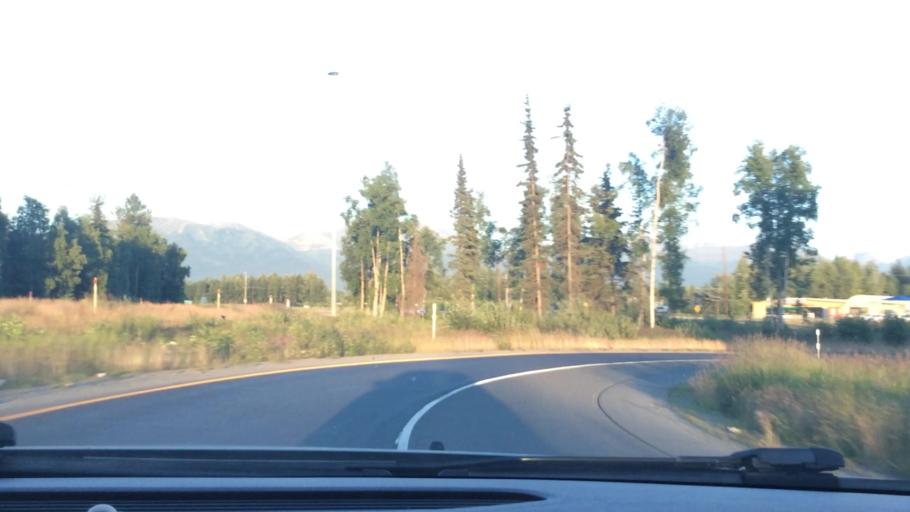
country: US
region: Alaska
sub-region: Anchorage Municipality
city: Anchorage
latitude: 61.2259
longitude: -149.7764
